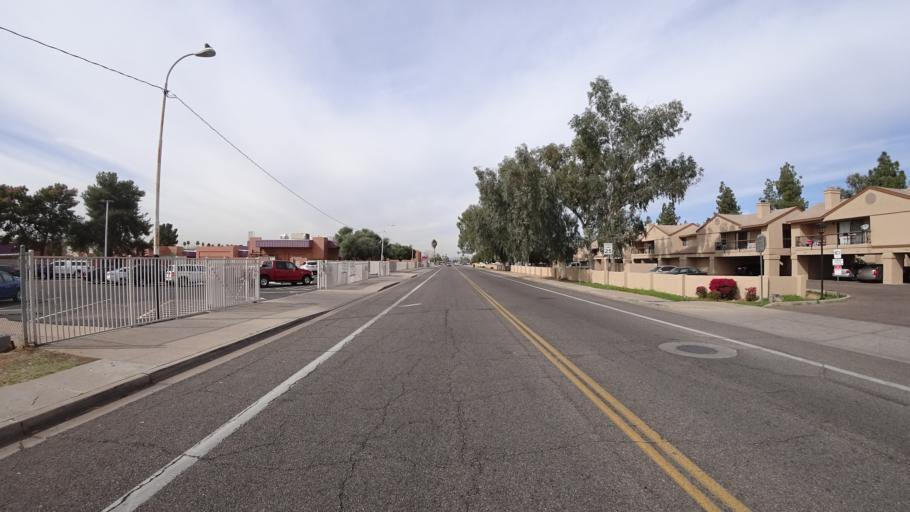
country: US
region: Arizona
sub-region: Maricopa County
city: Glendale
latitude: 33.5312
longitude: -112.1617
